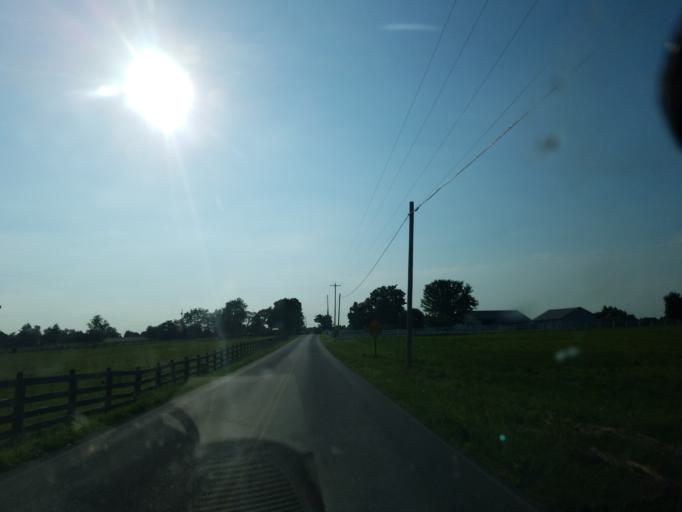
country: US
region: Ohio
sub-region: Adams County
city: West Union
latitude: 38.8778
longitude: -83.4867
